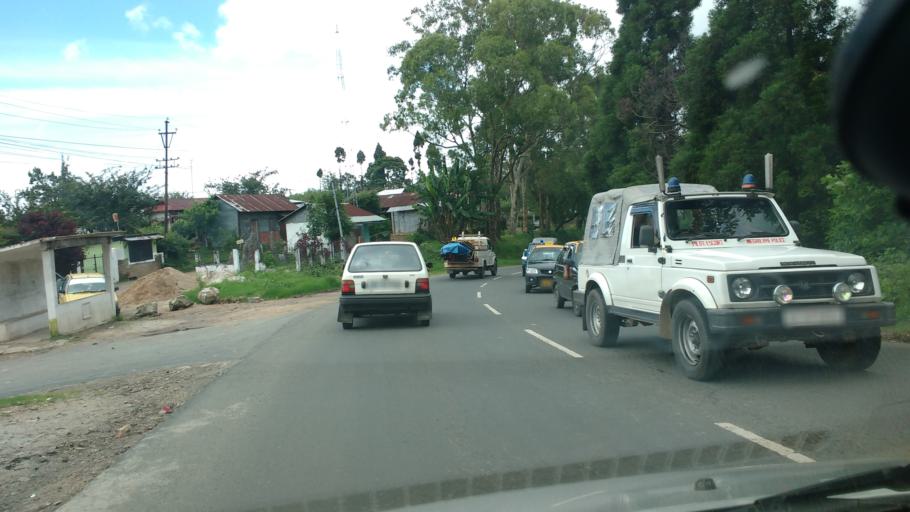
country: IN
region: Meghalaya
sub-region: East Khasi Hills
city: Shillong
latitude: 25.5565
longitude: 91.8473
